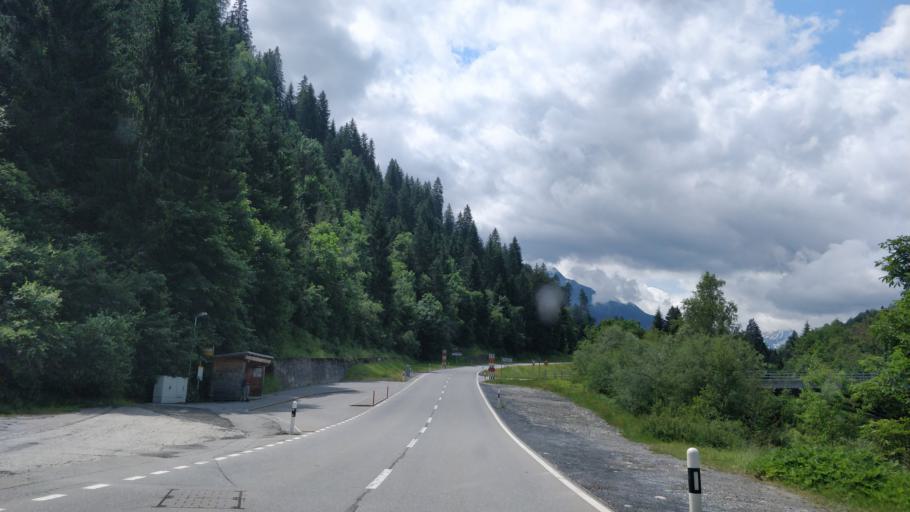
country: CH
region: Grisons
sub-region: Surselva District
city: Ilanz
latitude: 46.7169
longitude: 9.2001
